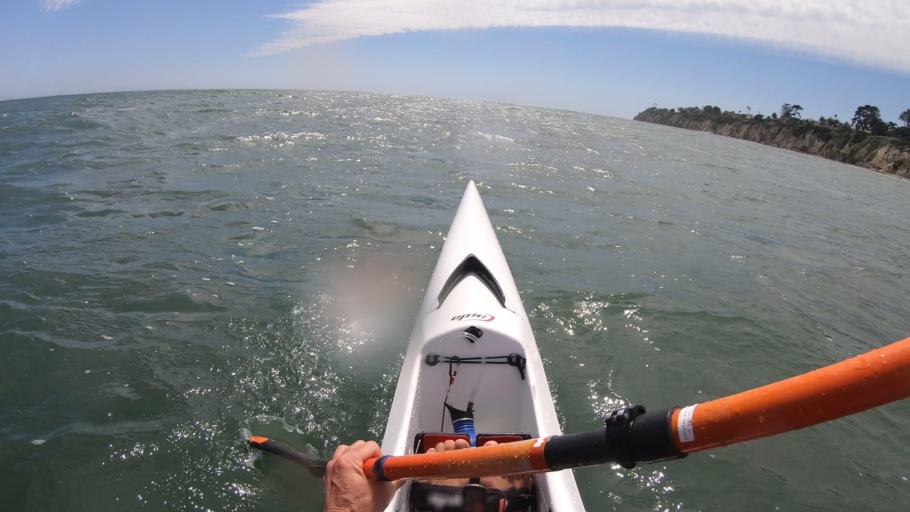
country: US
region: California
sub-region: Santa Barbara County
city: Santa Barbara
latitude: 34.3938
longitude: -119.7108
